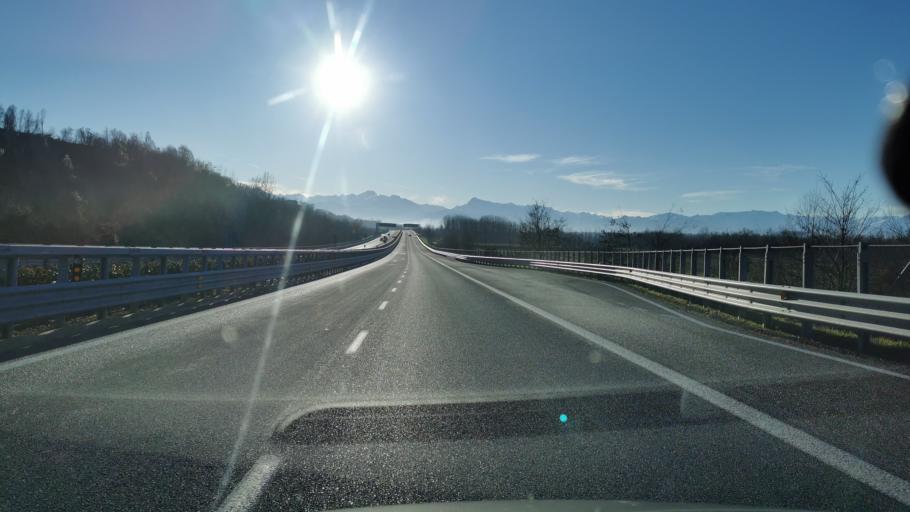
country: IT
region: Piedmont
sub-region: Provincia di Cuneo
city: Montanera
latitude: 44.4738
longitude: 7.6756
